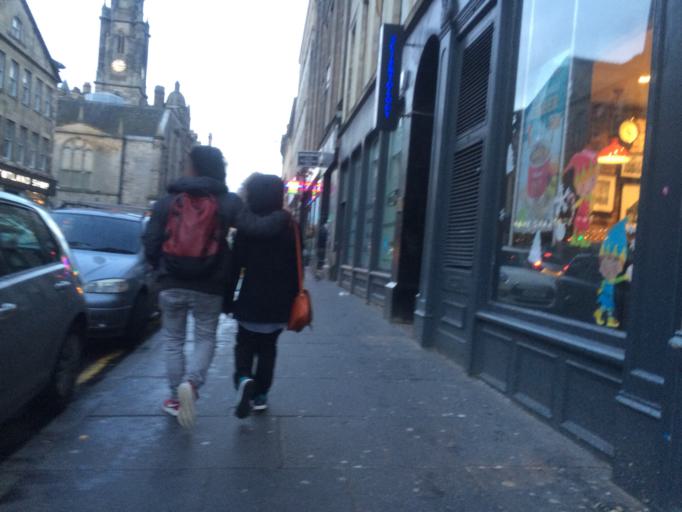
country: GB
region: Scotland
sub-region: Edinburgh
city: Edinburgh
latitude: 55.9492
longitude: -3.1869
